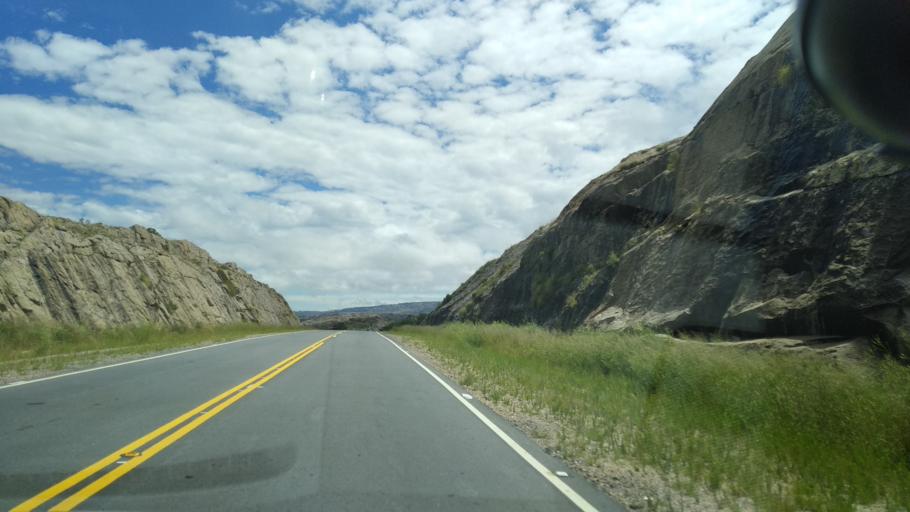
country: AR
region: Cordoba
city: Mina Clavero
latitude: -31.7301
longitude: -64.9007
